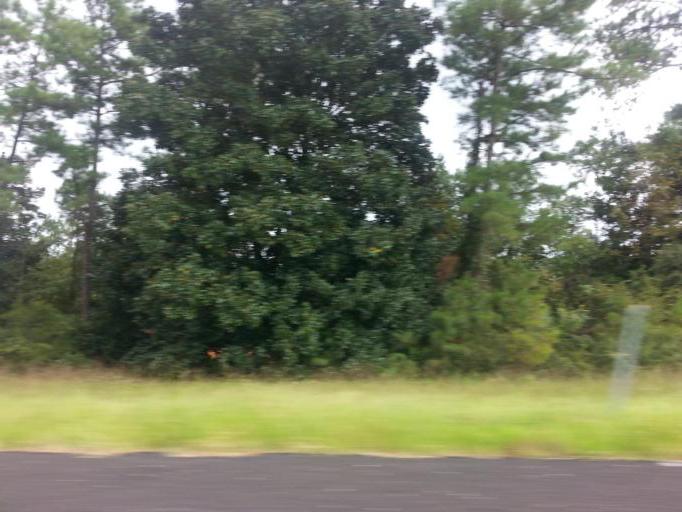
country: US
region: Alabama
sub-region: Conecuh County
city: Evergreen
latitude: 31.3326
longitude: -87.1213
